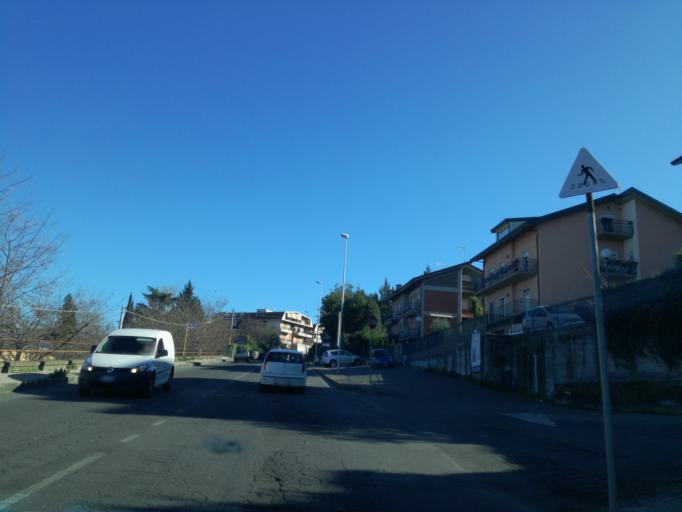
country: IT
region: Sicily
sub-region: Catania
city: Bronte
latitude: 37.7819
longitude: 14.8316
